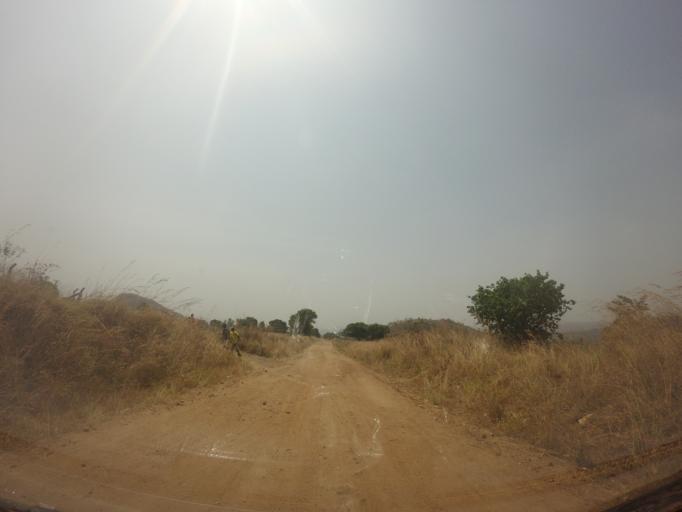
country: UG
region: Northern Region
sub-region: Arua District
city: Arua
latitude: 2.9328
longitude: 30.9826
